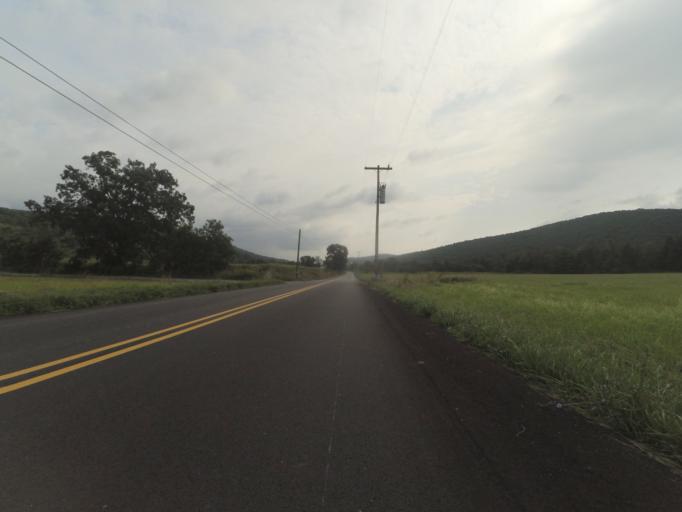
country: US
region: Pennsylvania
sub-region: Centre County
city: Milesburg
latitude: 41.0431
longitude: -77.7163
